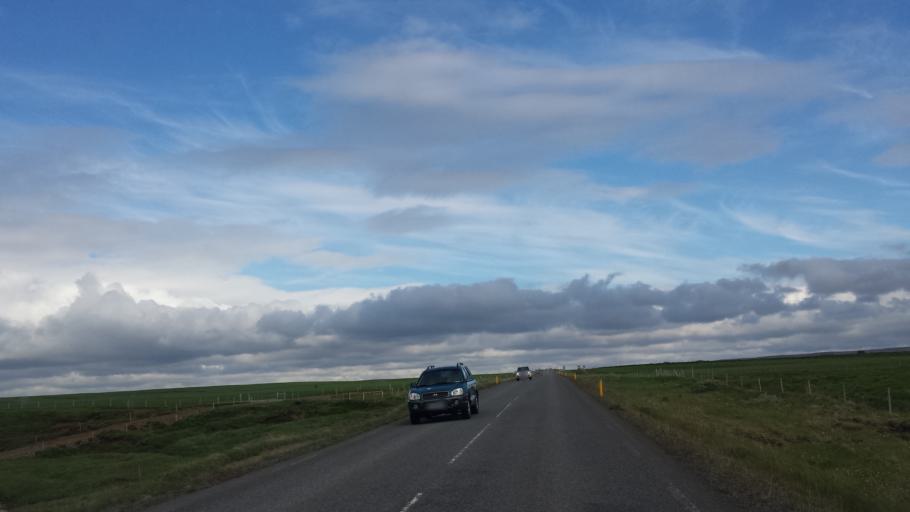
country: IS
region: South
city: Selfoss
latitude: 64.3091
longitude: -20.2245
